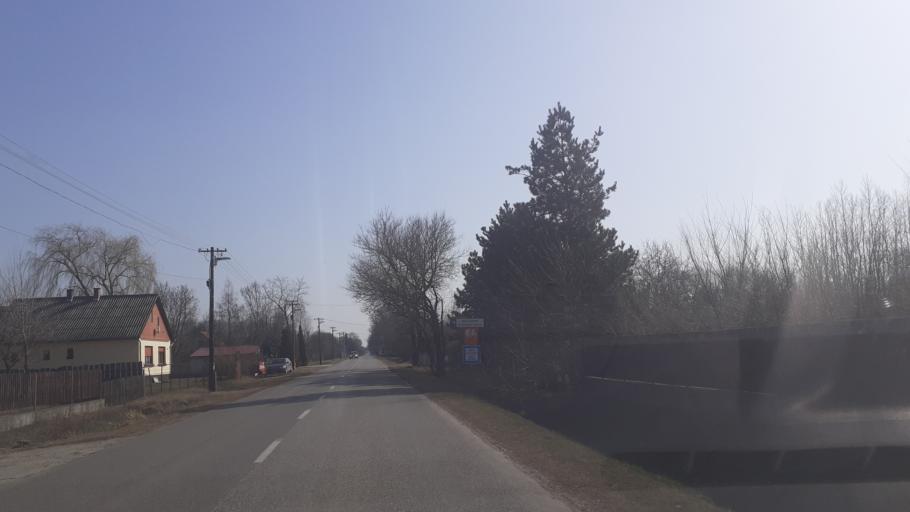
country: HU
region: Pest
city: Taborfalva
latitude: 47.0382
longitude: 19.4452
